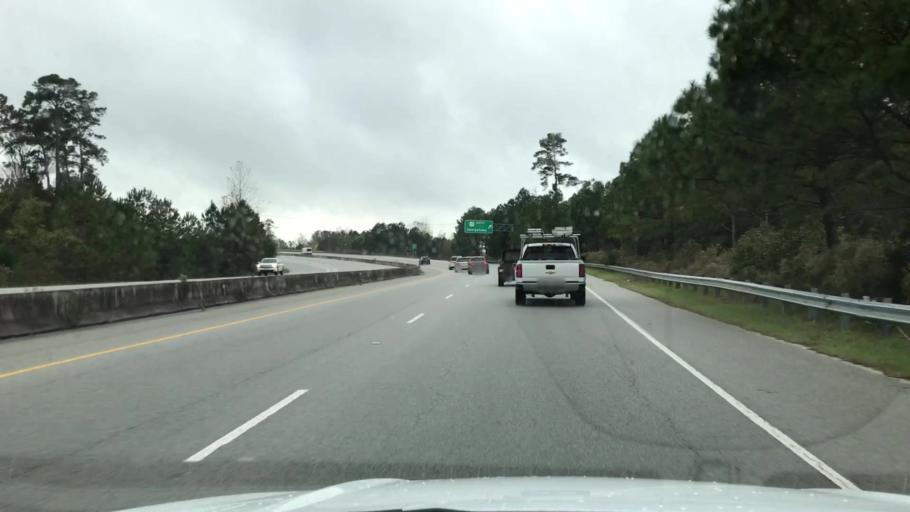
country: US
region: South Carolina
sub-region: Horry County
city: Myrtle Beach
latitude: 33.7435
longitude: -78.8495
